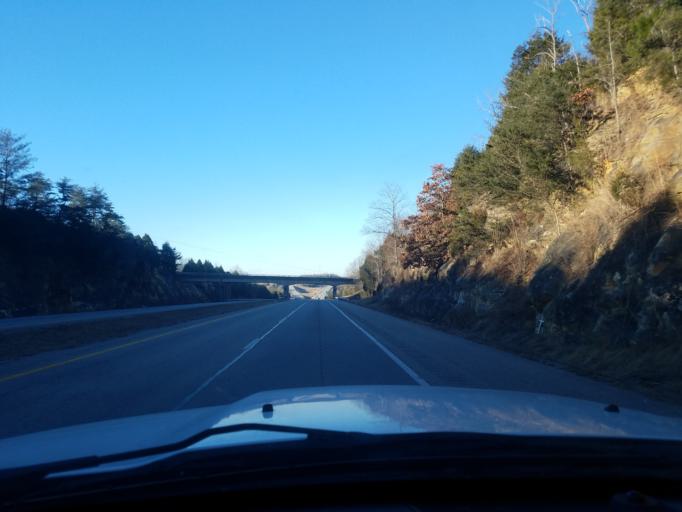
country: US
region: Kentucky
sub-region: Grayson County
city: Leitchfield
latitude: 37.4744
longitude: -86.2507
